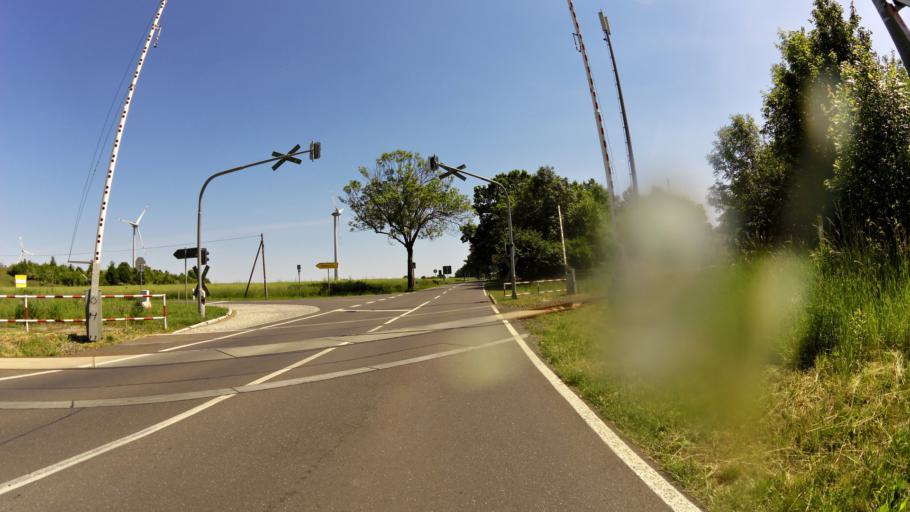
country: DE
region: Brandenburg
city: Lebus
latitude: 52.4402
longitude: 14.4707
